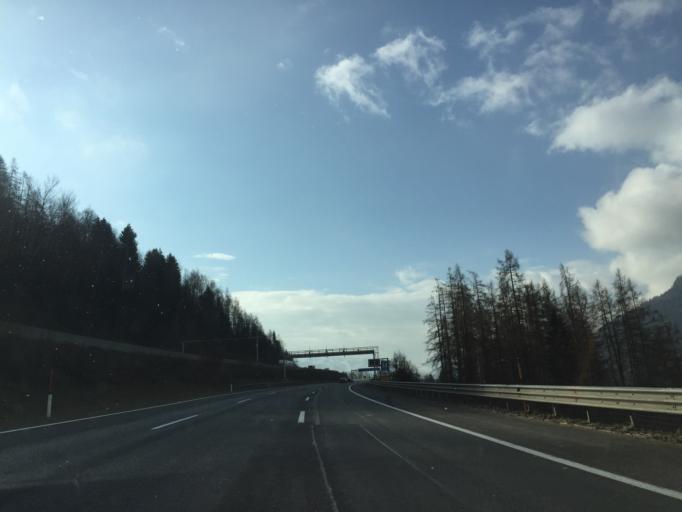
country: AT
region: Salzburg
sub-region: Politischer Bezirk Sankt Johann im Pongau
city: Pfarrwerfen
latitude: 47.4499
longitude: 13.2178
